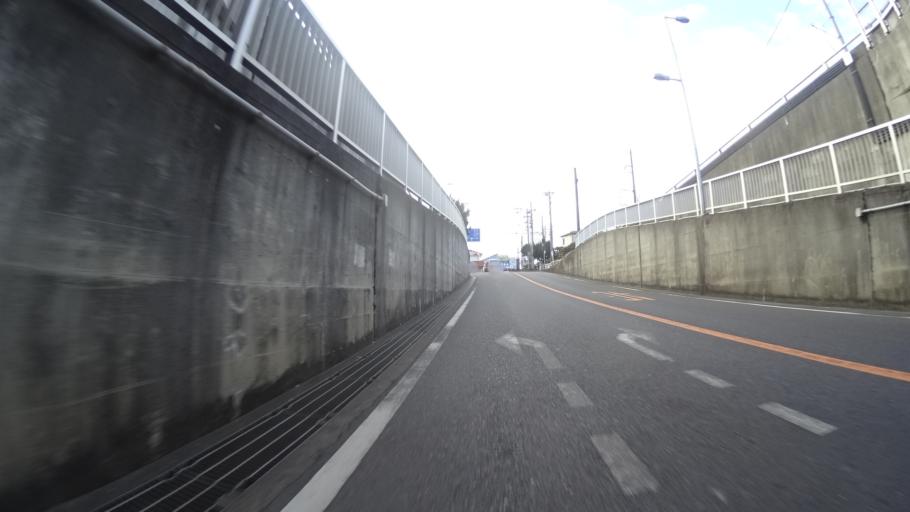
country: JP
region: Kanagawa
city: Ninomiya
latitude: 35.3054
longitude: 139.2774
